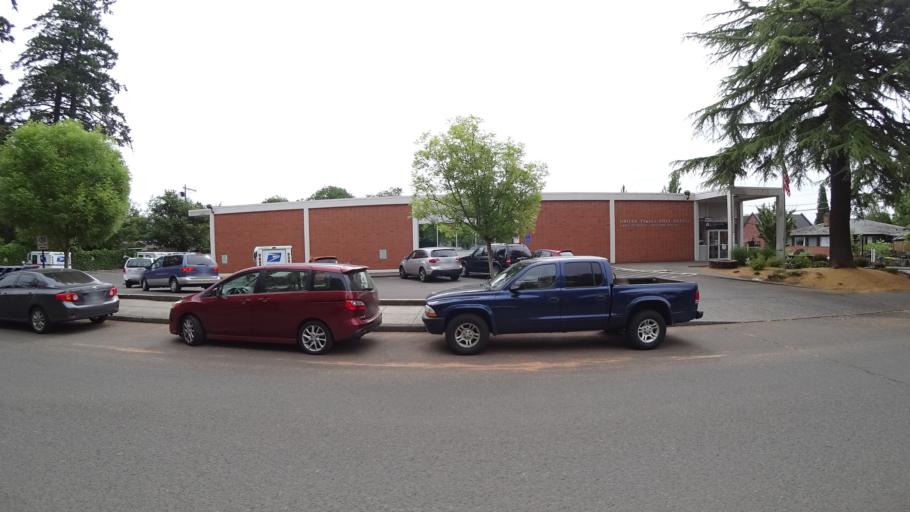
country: US
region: Oregon
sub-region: Clackamas County
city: Lake Oswego
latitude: 45.4214
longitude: -122.6676
